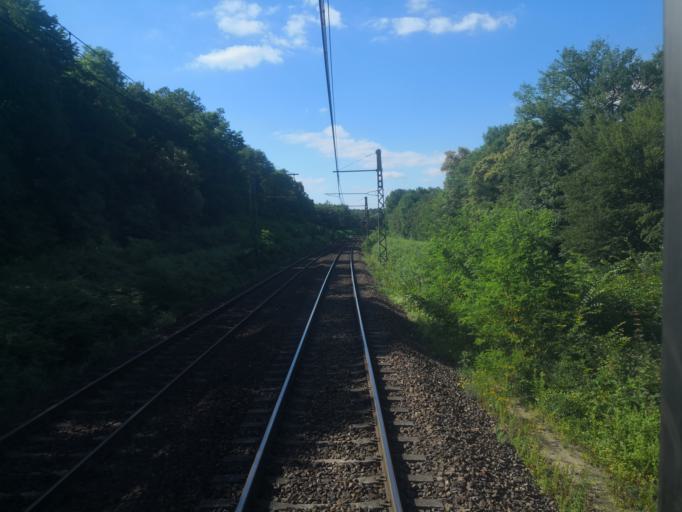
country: FR
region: Ile-de-France
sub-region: Departement de Seine-et-Marne
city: La Rochette
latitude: 48.4896
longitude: 2.6725
